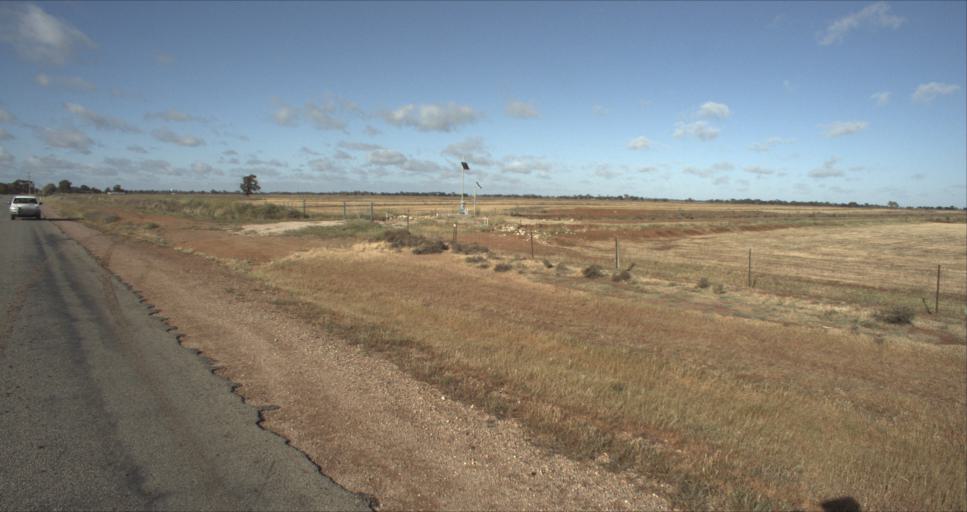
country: AU
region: New South Wales
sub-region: Leeton
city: Leeton
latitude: -34.5097
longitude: 146.3925
